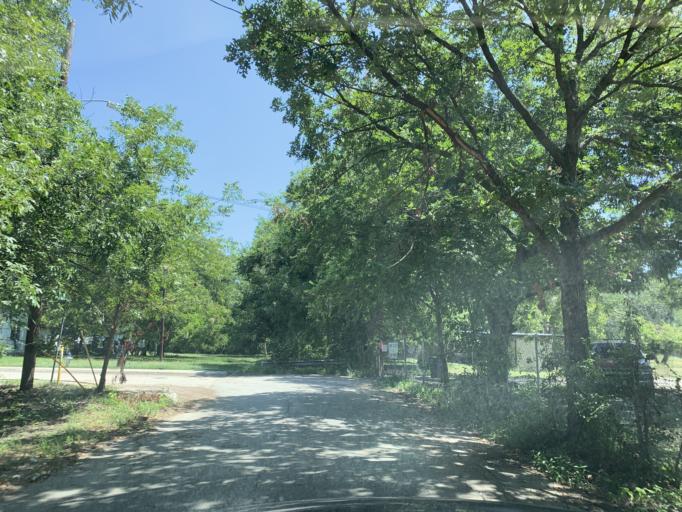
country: US
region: Texas
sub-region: Dallas County
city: Hutchins
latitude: 32.6825
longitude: -96.7936
